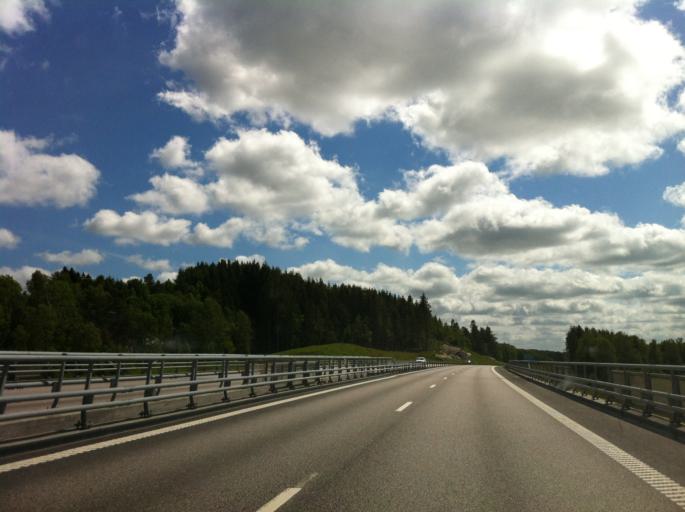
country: SE
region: Vaestra Goetaland
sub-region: Lilla Edets Kommun
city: Lodose
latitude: 58.0235
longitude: 12.1768
